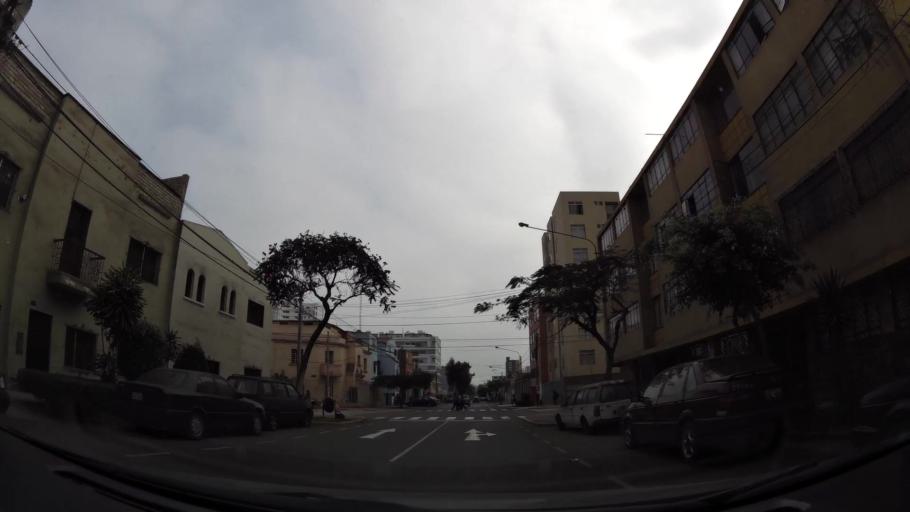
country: PE
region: Lima
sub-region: Lima
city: San Isidro
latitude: -12.0829
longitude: -77.0379
